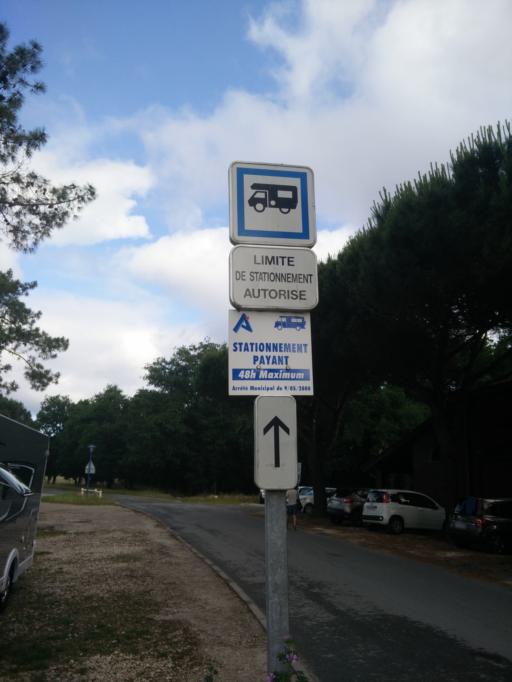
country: FR
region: Aquitaine
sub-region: Departement de la Gironde
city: Andernos-les-Bains
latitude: 44.7447
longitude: -1.1096
